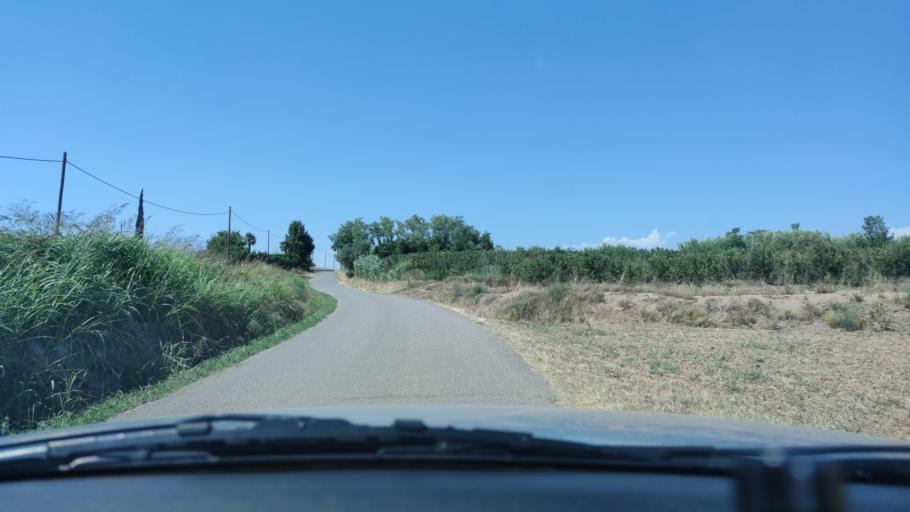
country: ES
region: Catalonia
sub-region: Provincia de Lleida
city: Torrefarrera
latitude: 41.6653
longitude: 0.6197
